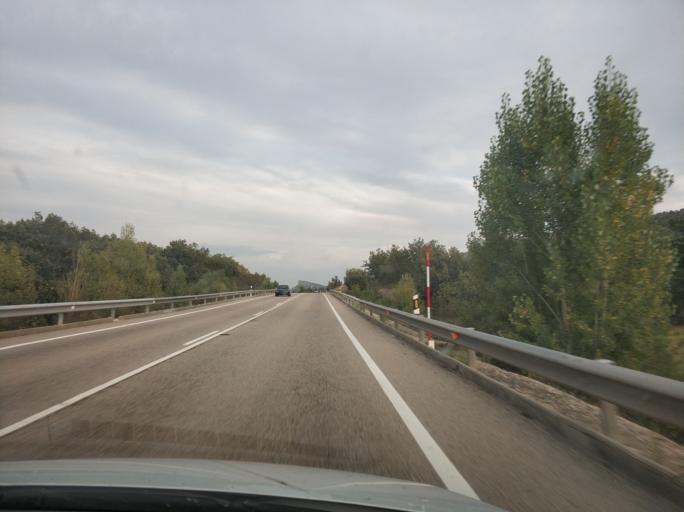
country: ES
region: Castille and Leon
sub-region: Provincia de Burgos
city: Mambrillas de Lara
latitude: 42.0939
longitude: -3.4837
